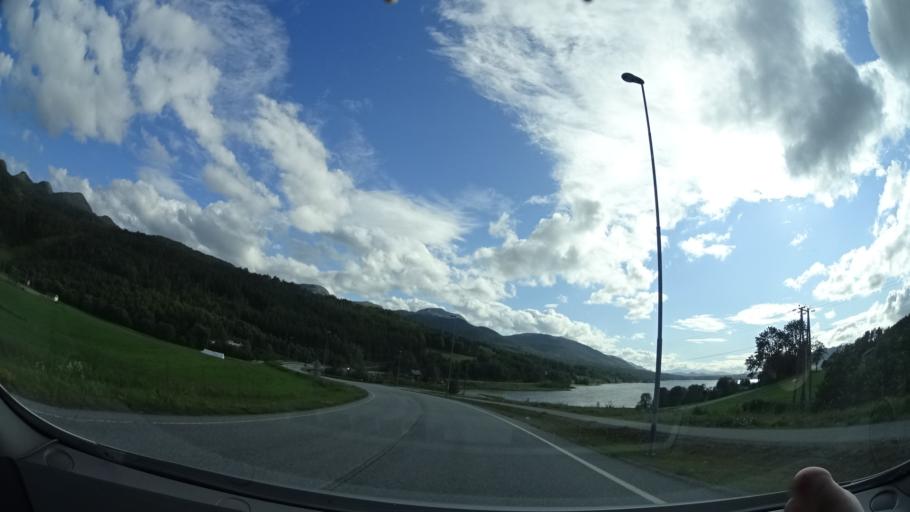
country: NO
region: More og Romsdal
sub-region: Halsa
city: Liaboen
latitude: 63.0893
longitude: 8.3540
